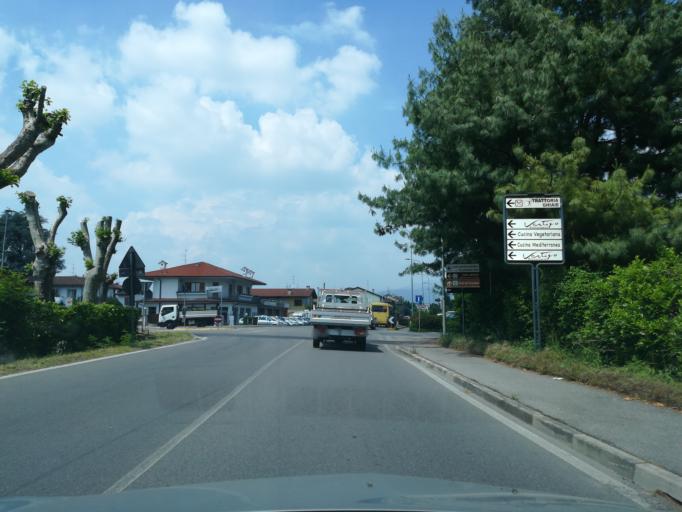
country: IT
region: Lombardy
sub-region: Provincia di Bergamo
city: Seriate
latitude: 45.6735
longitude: 9.7336
